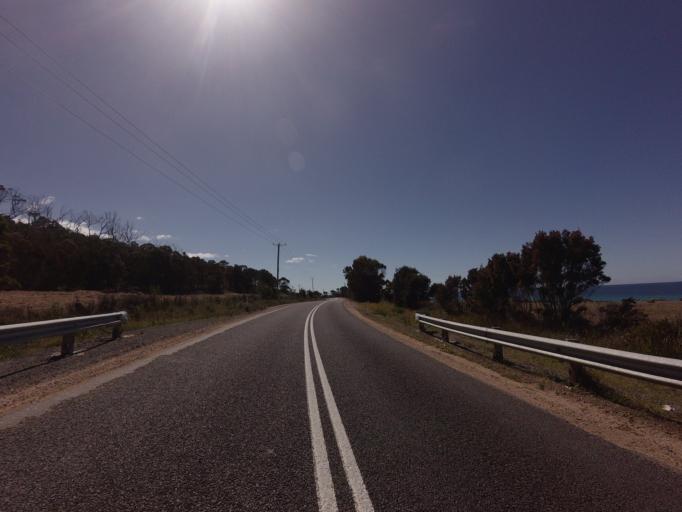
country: AU
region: Tasmania
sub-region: Break O'Day
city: St Helens
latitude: -41.7967
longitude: 148.2614
